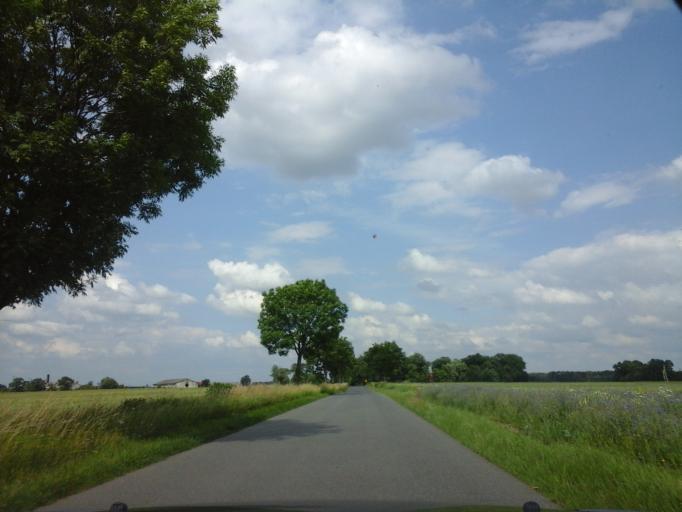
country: PL
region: West Pomeranian Voivodeship
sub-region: Powiat choszczenski
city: Pelczyce
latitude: 53.0697
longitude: 15.3702
